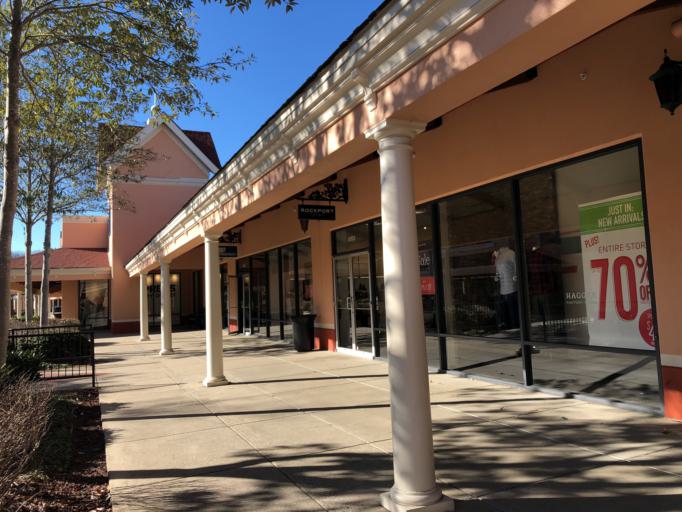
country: US
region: Georgia
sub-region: Dawson County
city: Dawsonville
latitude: 34.3591
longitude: -84.0475
